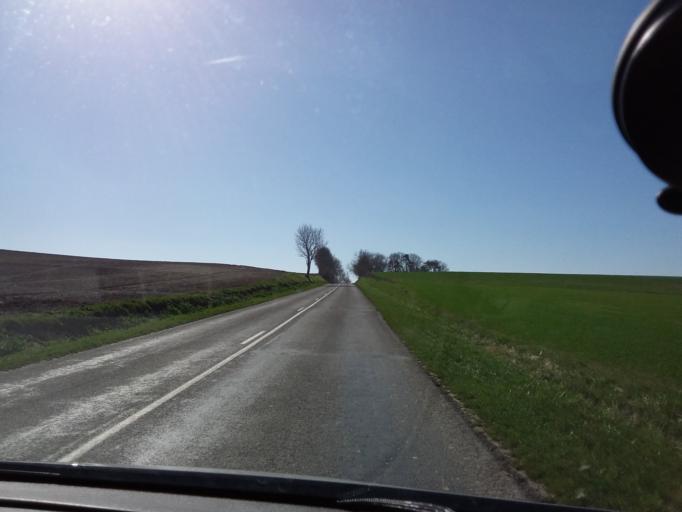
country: FR
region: Picardie
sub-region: Departement de l'Aisne
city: Montcornet
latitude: 49.6434
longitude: 4.0213
